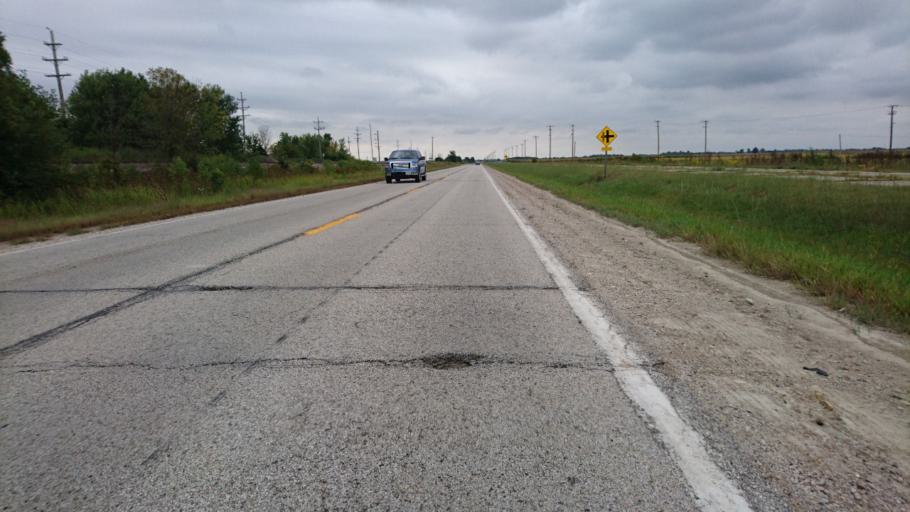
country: US
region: Illinois
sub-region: Livingston County
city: Pontiac
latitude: 40.9202
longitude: -88.6028
